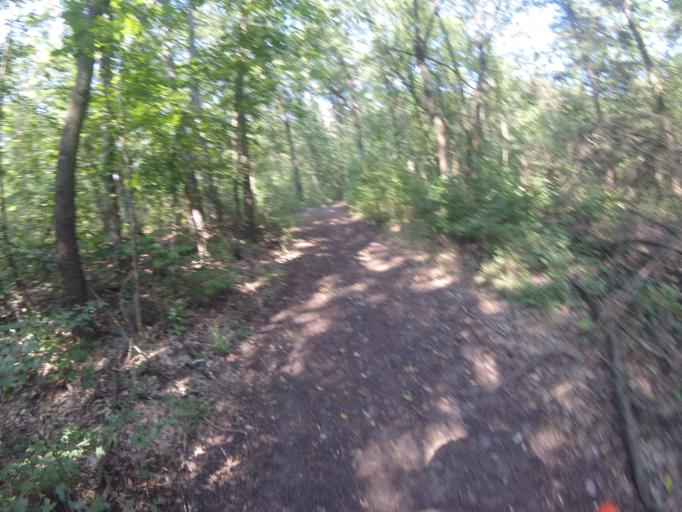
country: HU
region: Nograd
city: Bujak
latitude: 47.8869
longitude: 19.5337
